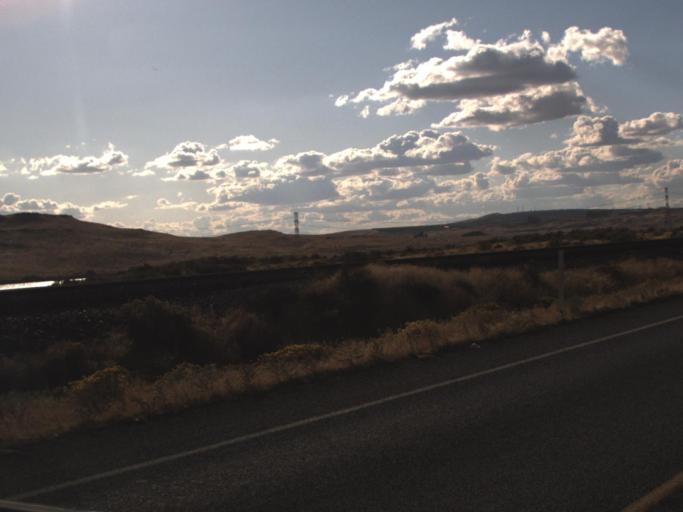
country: US
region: Oregon
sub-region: Morrow County
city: Boardman
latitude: 45.8661
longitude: -119.8078
